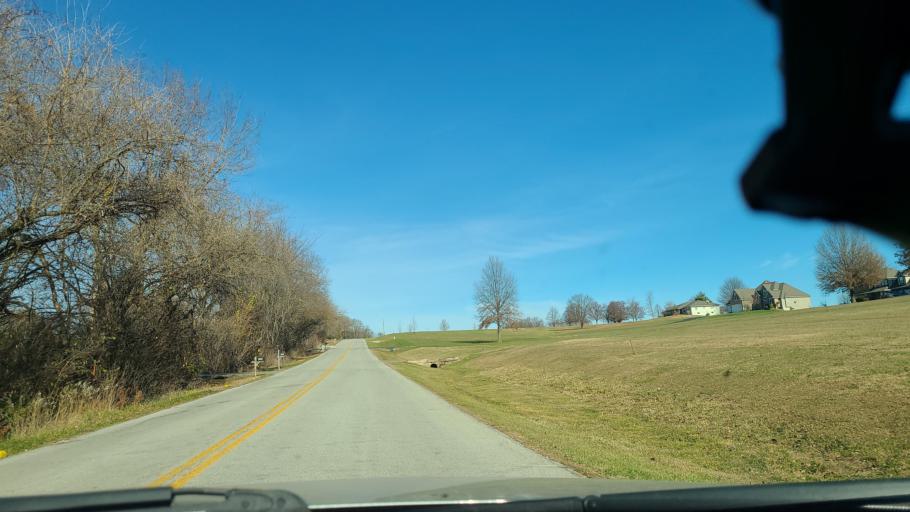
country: US
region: Kansas
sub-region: Leavenworth County
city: Lansing
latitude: 39.1943
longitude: -94.8639
